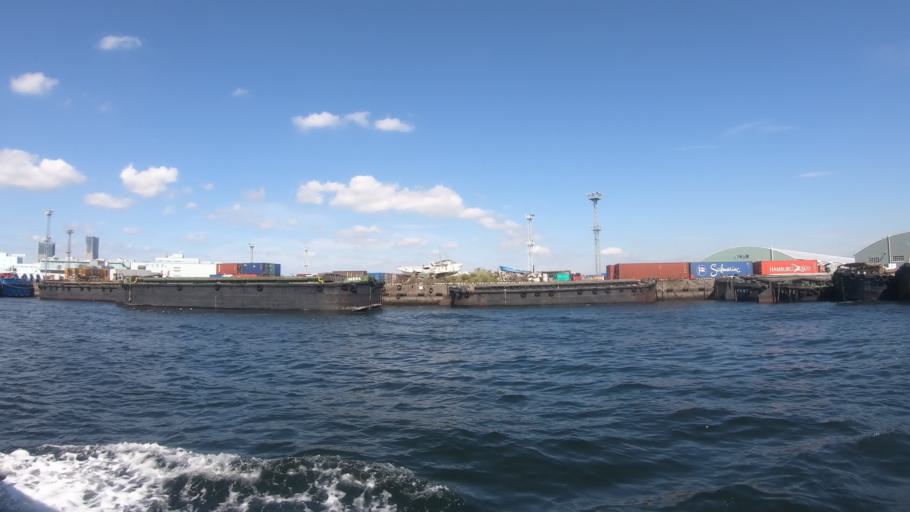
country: JP
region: Kanagawa
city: Yokohama
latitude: 35.4457
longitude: 139.6625
